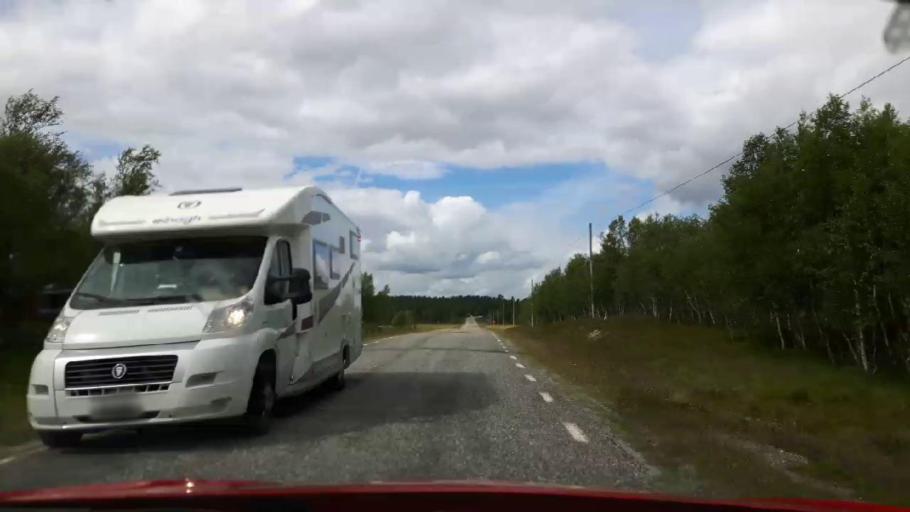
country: NO
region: Hedmark
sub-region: Engerdal
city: Engerdal
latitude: 62.2937
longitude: 12.8126
